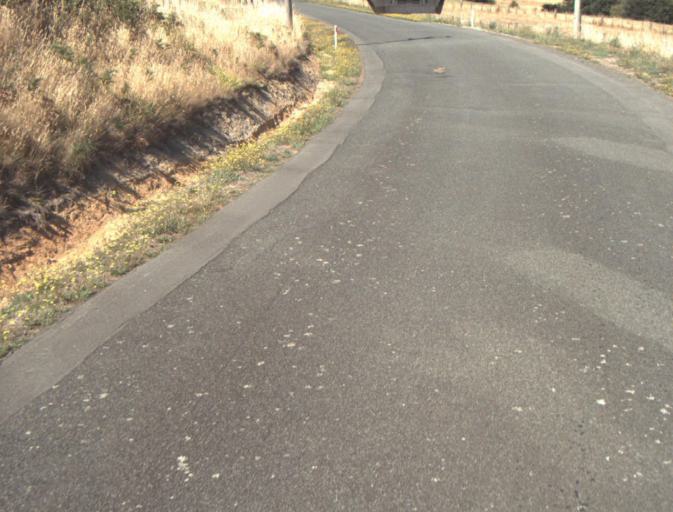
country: AU
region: Tasmania
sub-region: Launceston
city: Newstead
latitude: -41.3460
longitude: 147.3028
